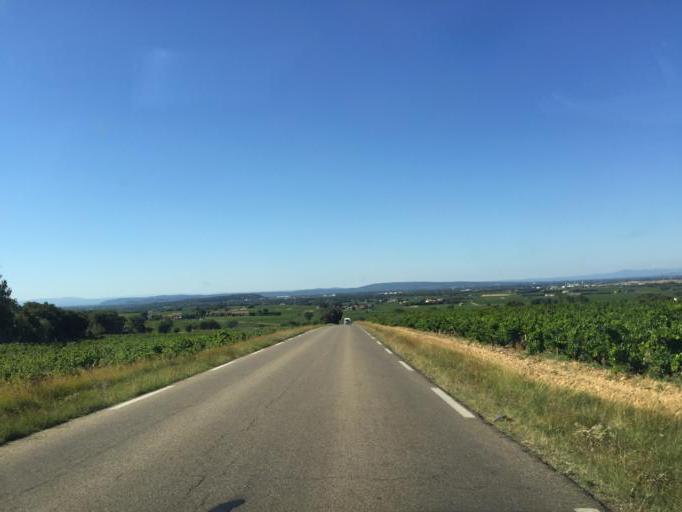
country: FR
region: Provence-Alpes-Cote d'Azur
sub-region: Departement du Vaucluse
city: Chateauneuf-du-Pape
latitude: 44.0838
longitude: 4.8315
